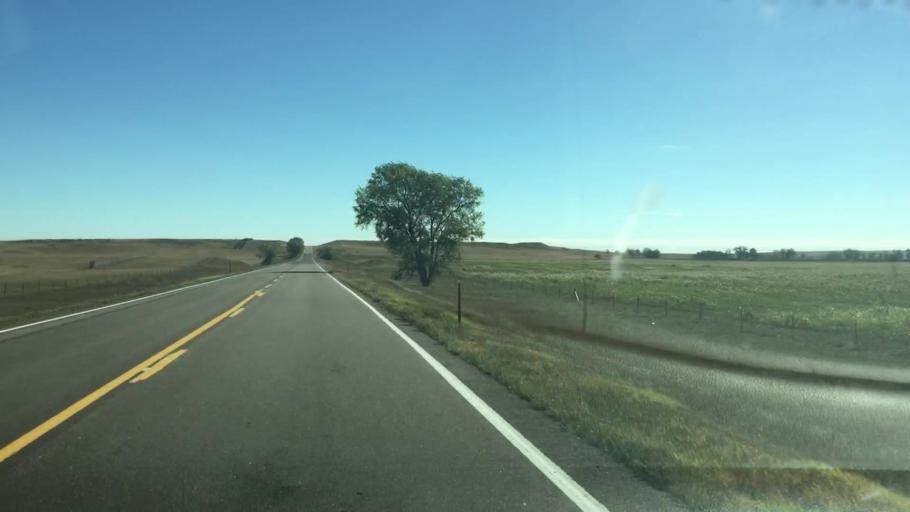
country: US
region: Colorado
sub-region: Lincoln County
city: Limon
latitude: 39.2948
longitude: -103.8927
